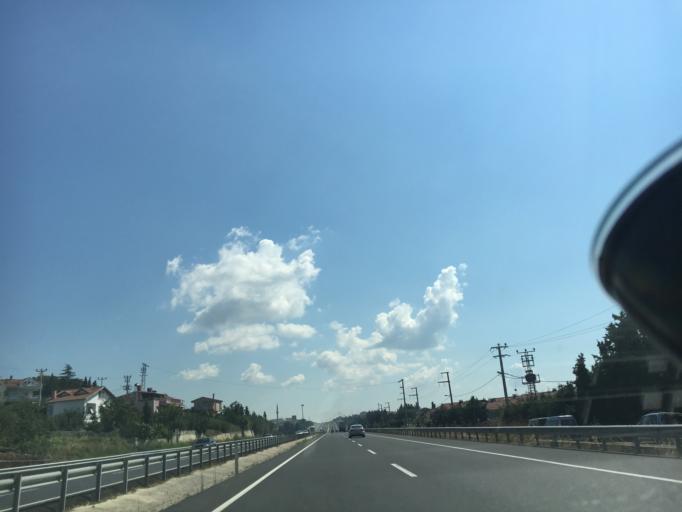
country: TR
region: Istanbul
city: Canta
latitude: 41.0583
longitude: 28.0779
